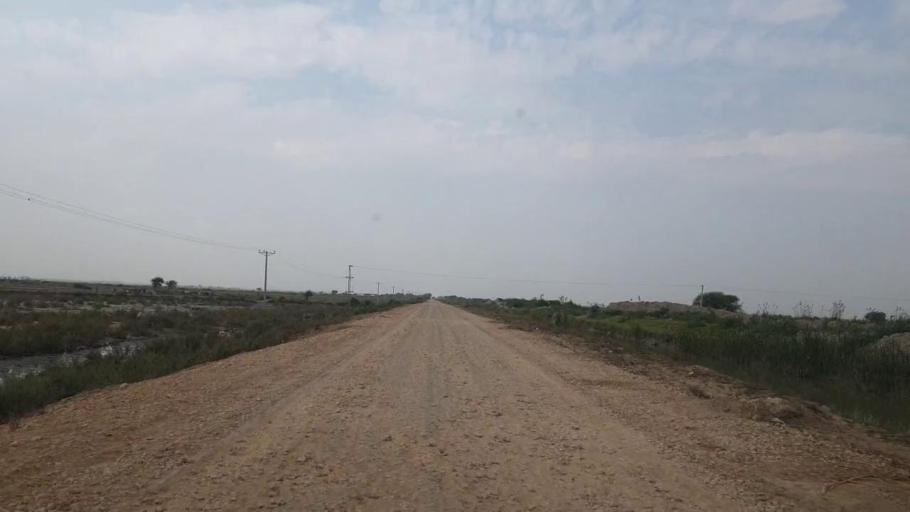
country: PK
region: Sindh
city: Kario
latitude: 24.6155
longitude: 68.5875
